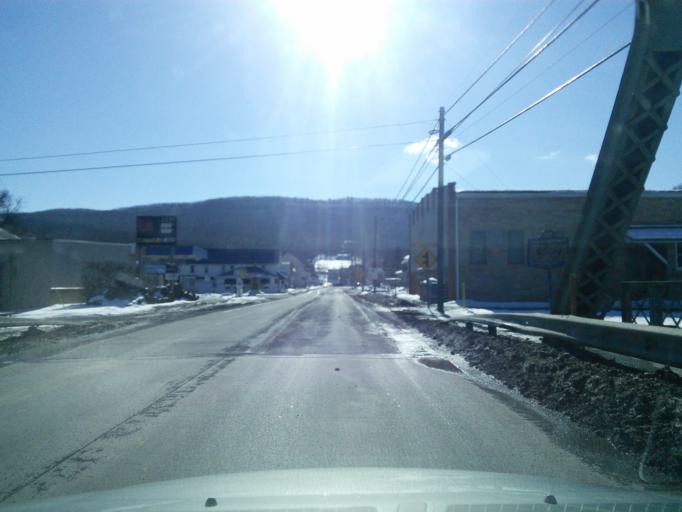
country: US
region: Pennsylvania
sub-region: Centre County
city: Milesburg
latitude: 40.9431
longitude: -77.7868
